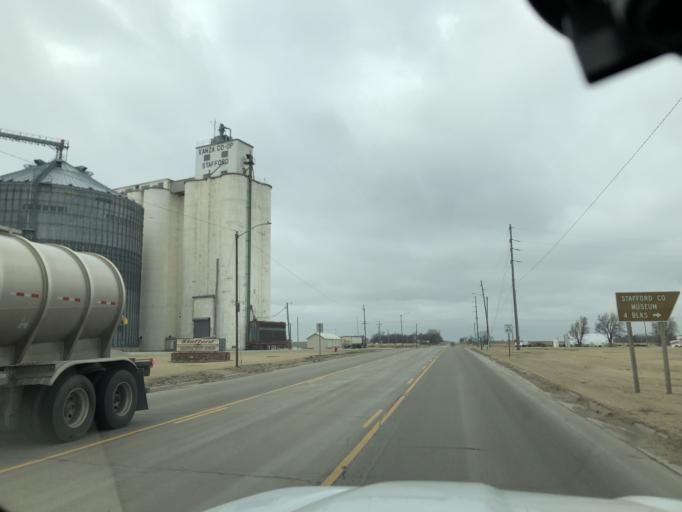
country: US
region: Kansas
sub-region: Stafford County
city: Stafford
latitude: 37.9549
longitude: -98.5980
